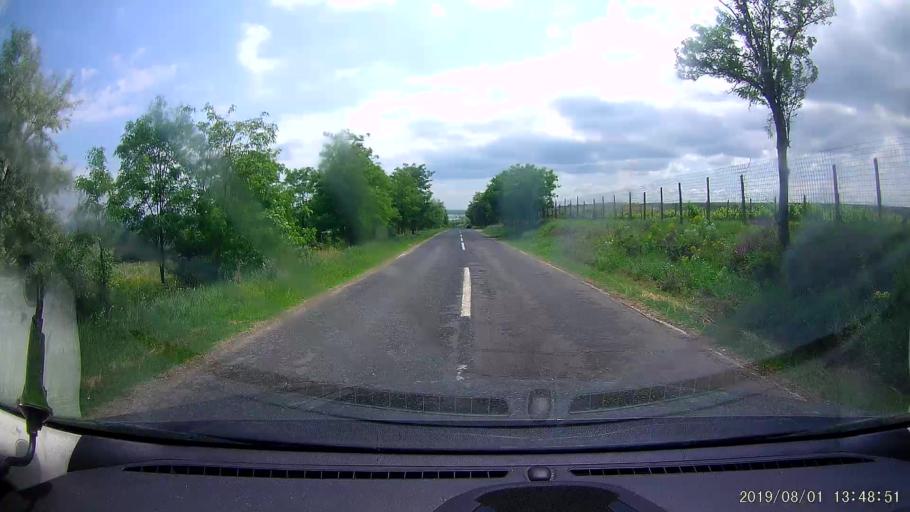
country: RO
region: Galati
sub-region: Comuna Oancea
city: Oancea
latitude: 45.9018
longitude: 28.1094
